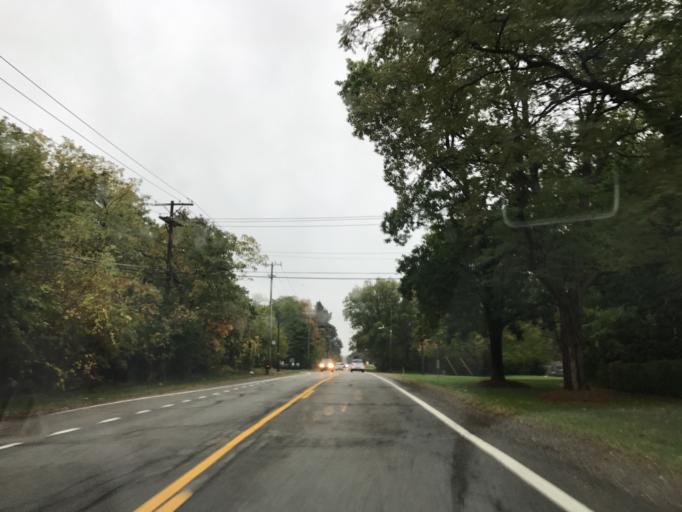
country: US
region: Michigan
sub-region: Oakland County
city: Franklin
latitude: 42.4998
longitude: -83.3318
